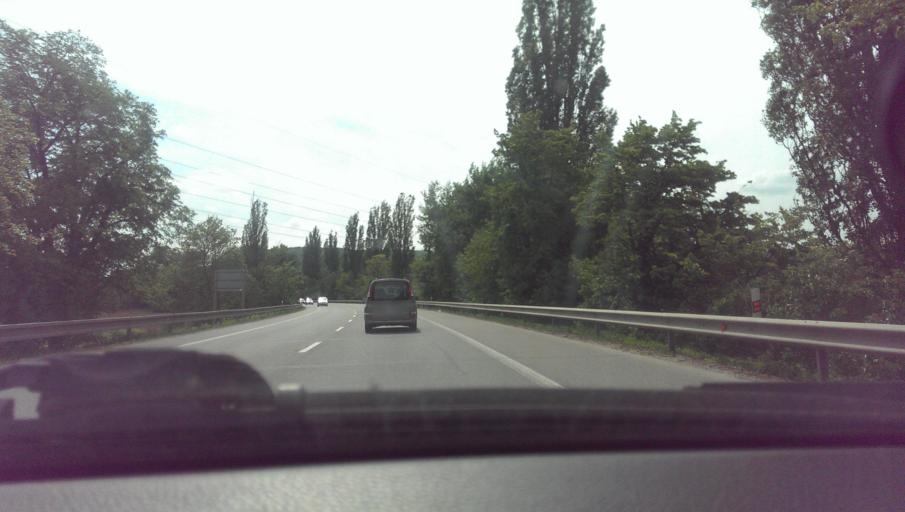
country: CZ
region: Zlin
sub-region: Okres Zlin
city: Napajedla
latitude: 49.1823
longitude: 17.5115
